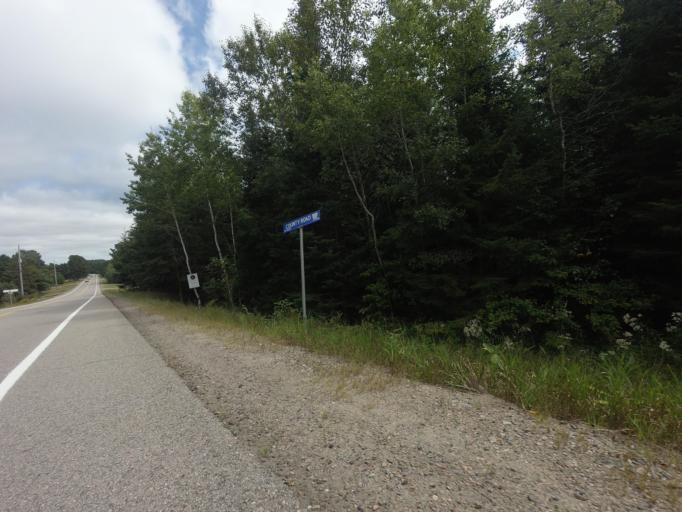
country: CA
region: Ontario
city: Bancroft
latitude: 44.9056
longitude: -78.4211
